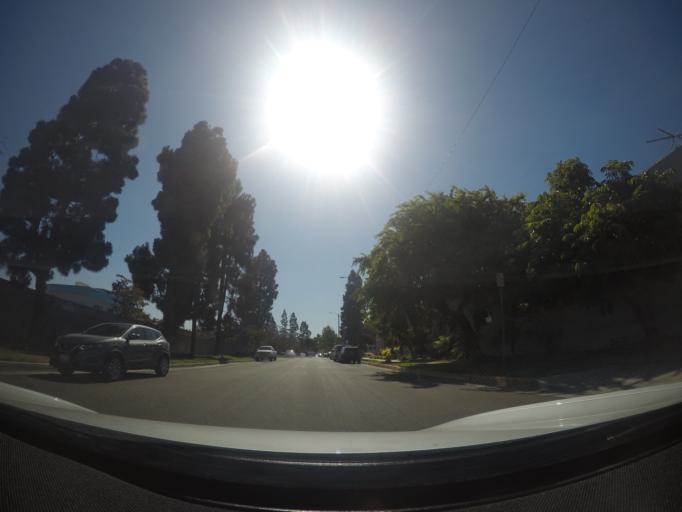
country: US
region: California
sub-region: Los Angeles County
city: Torrance
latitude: 33.8395
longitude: -118.3599
